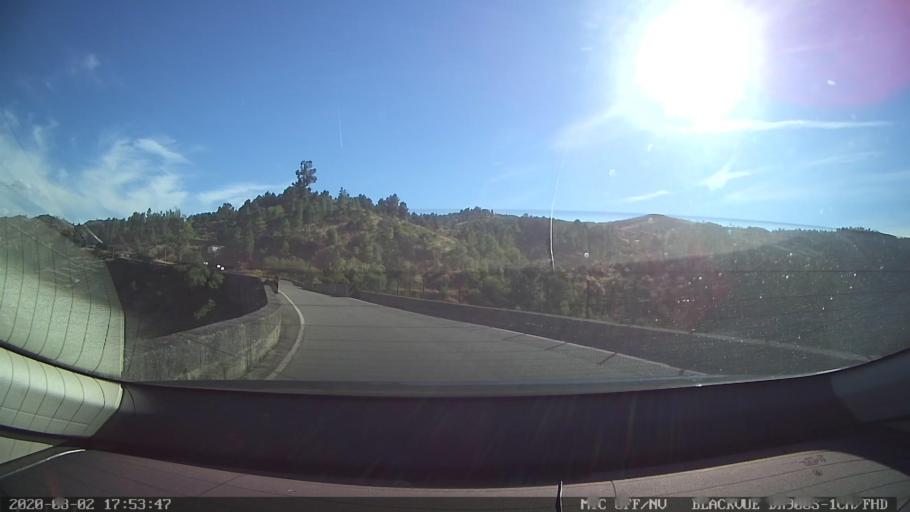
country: PT
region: Vila Real
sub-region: Murca
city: Murca
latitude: 41.4095
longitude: -7.4682
